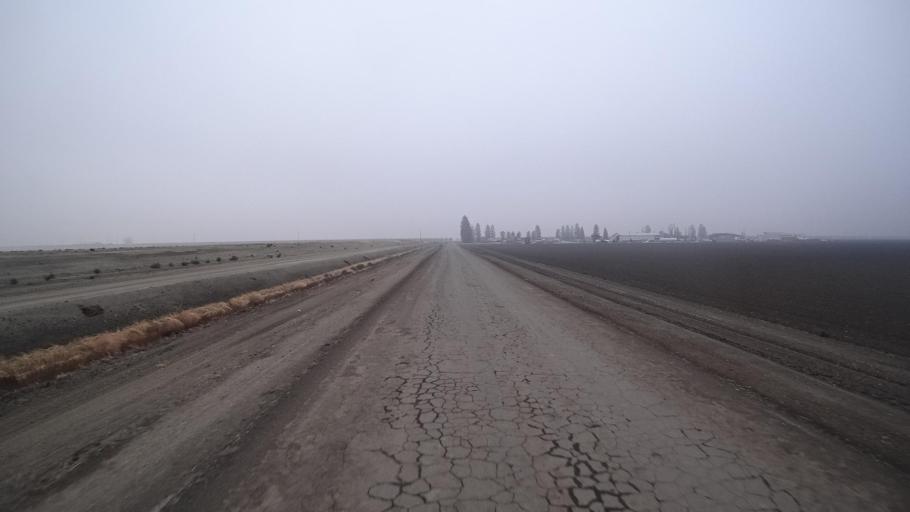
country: US
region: California
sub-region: Kern County
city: Buttonwillow
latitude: 35.4124
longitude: -119.5149
